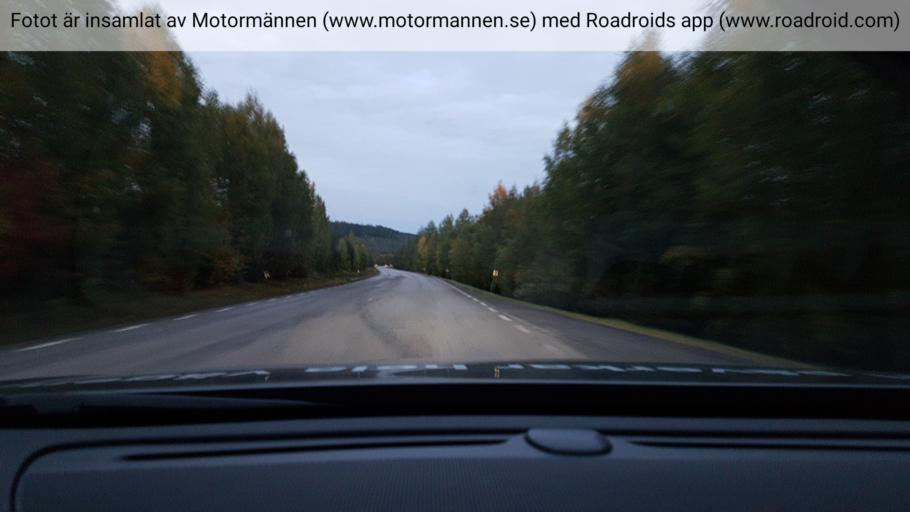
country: SE
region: Norrbotten
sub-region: Alvsbyns Kommun
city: AElvsbyn
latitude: 65.7817
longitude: 20.7807
